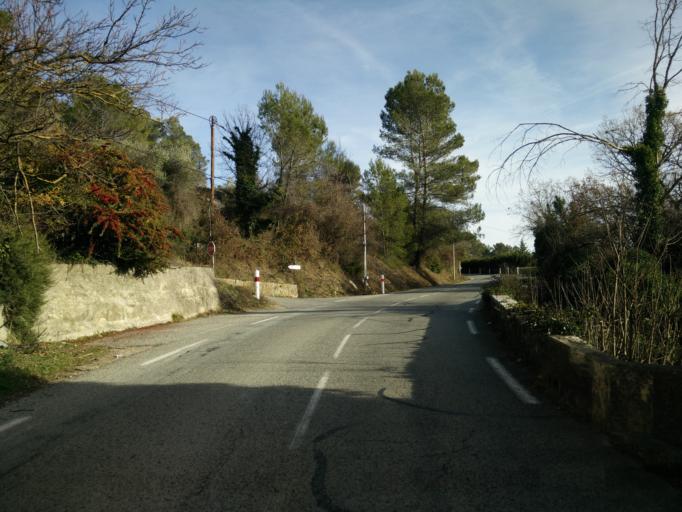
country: FR
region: Provence-Alpes-Cote d'Azur
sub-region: Departement du Var
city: Montauroux
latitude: 43.5971
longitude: 6.7941
